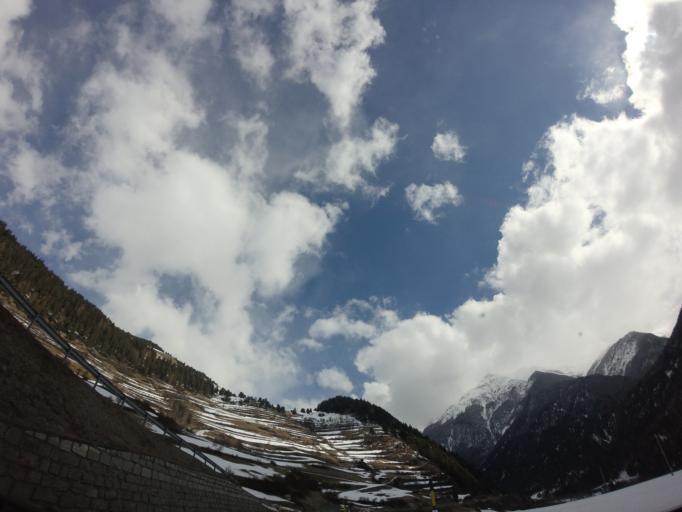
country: CH
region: Grisons
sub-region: Inn District
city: Scuol
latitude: 46.8328
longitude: 10.3867
